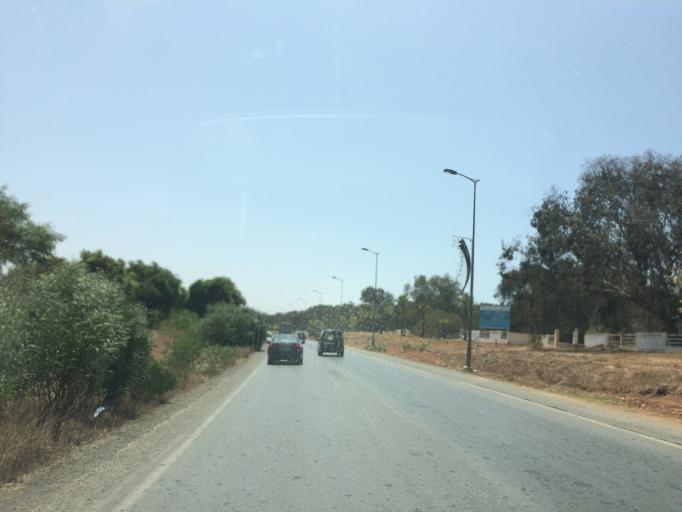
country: MA
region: Rabat-Sale-Zemmour-Zaer
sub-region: Skhirate-Temara
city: Temara
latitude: 33.9623
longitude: -6.9048
